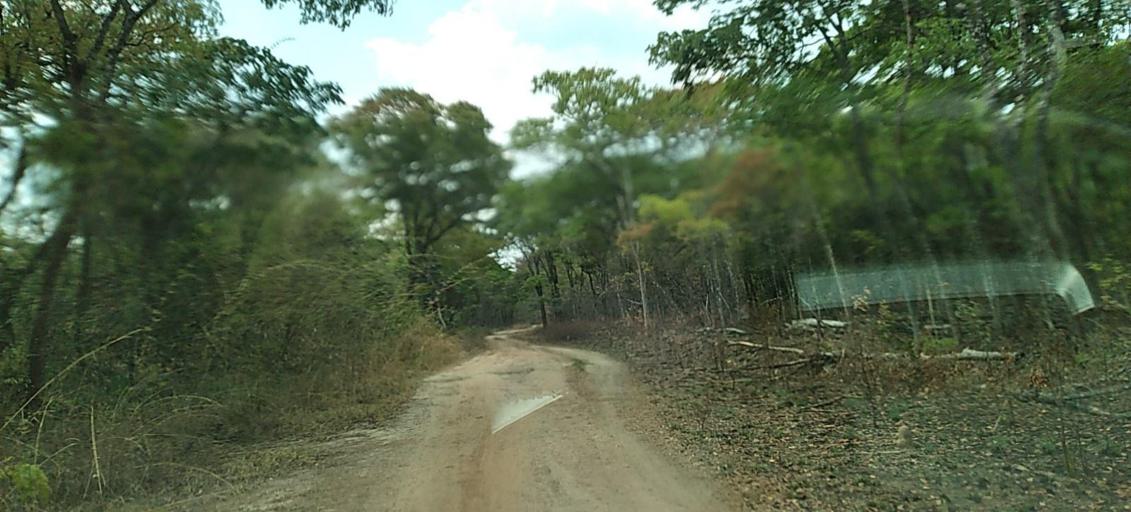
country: ZM
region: Copperbelt
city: Chingola
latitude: -12.7597
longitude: 27.7067
